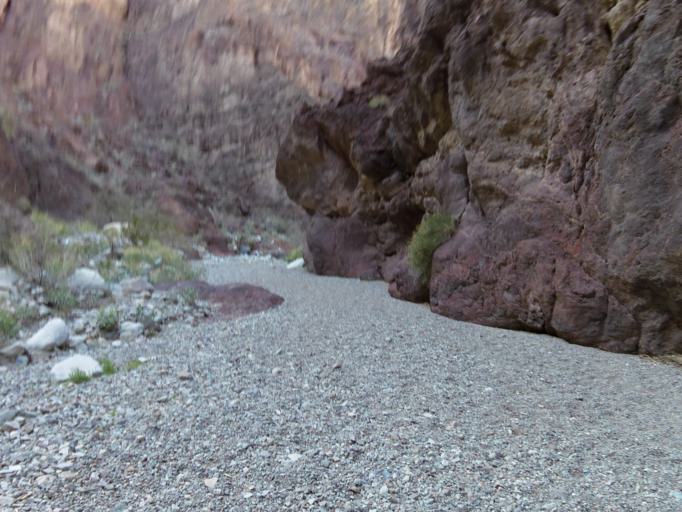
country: US
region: Nevada
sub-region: Clark County
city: Boulder City
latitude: 35.9720
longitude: -114.7166
